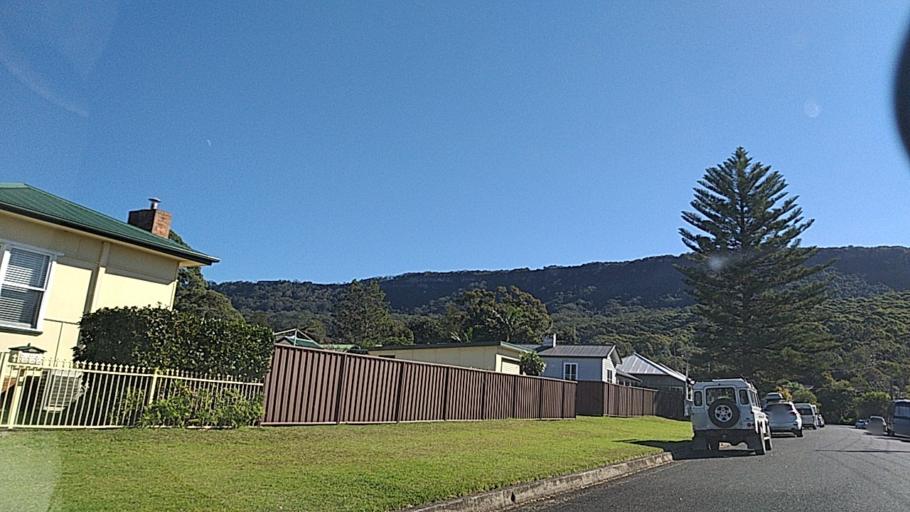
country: AU
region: New South Wales
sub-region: Wollongong
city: Bulli
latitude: -34.3125
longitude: 150.9261
